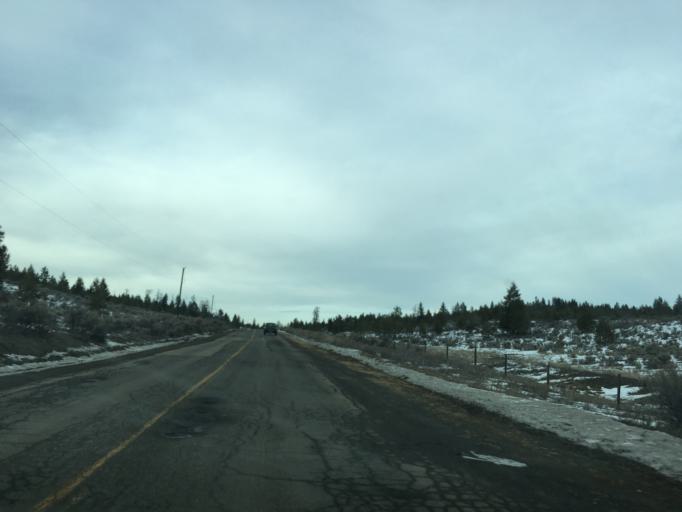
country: CA
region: British Columbia
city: Kamloops
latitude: 50.6332
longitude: -120.4453
